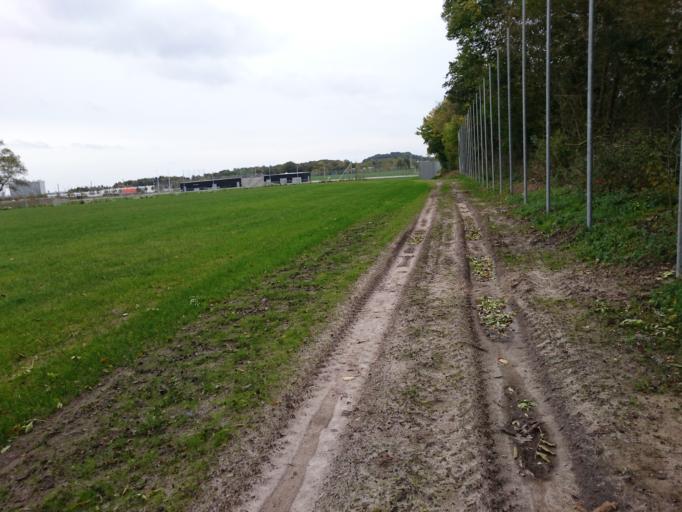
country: DK
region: Central Jutland
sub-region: Arhus Kommune
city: Stavtrup
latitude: 56.1185
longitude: 10.1234
